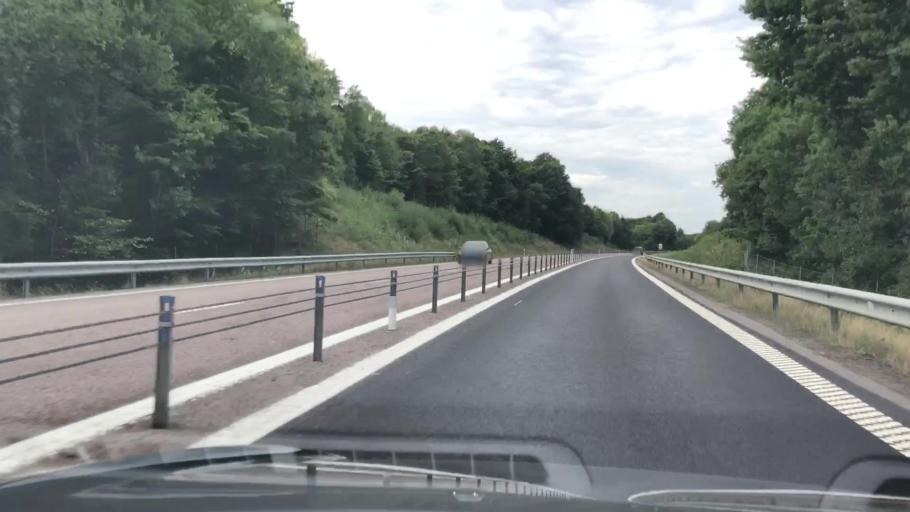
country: SE
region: Blekinge
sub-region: Ronneby Kommun
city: Brakne-Hoby
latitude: 56.2073
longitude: 15.0711
